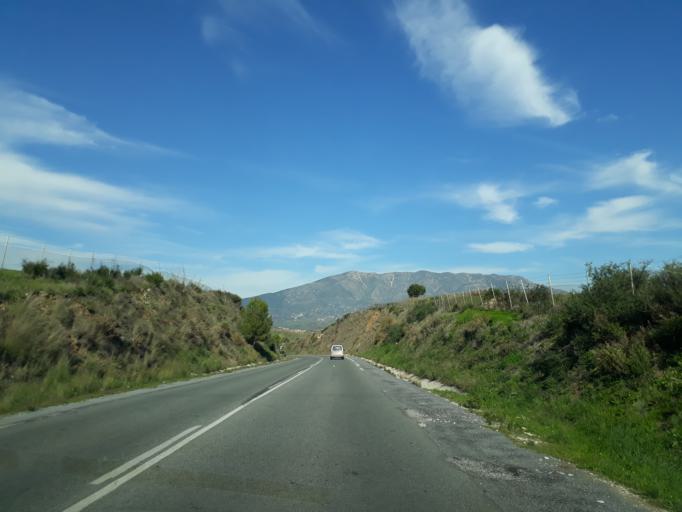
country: ES
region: Andalusia
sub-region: Provincia de Malaga
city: Fuengirola
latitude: 36.5345
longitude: -4.6859
